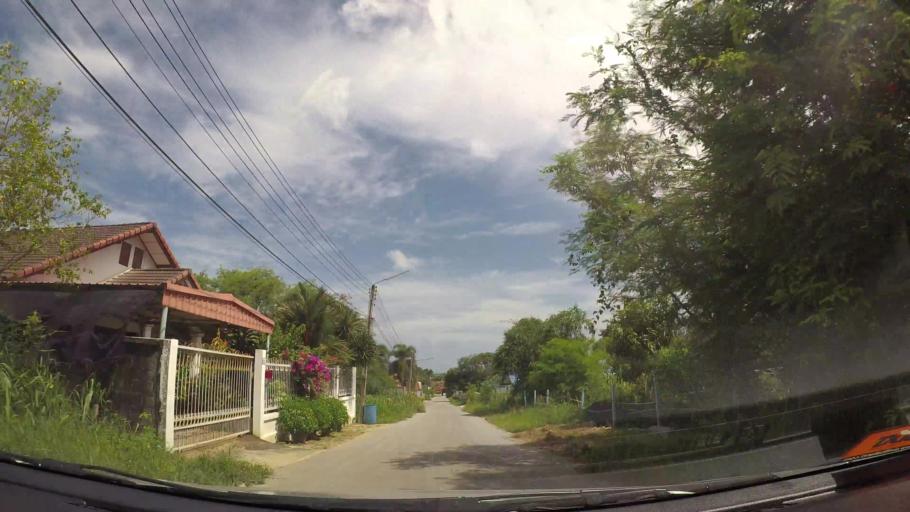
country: TH
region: Chon Buri
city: Sattahip
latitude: 12.6961
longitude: 100.9084
